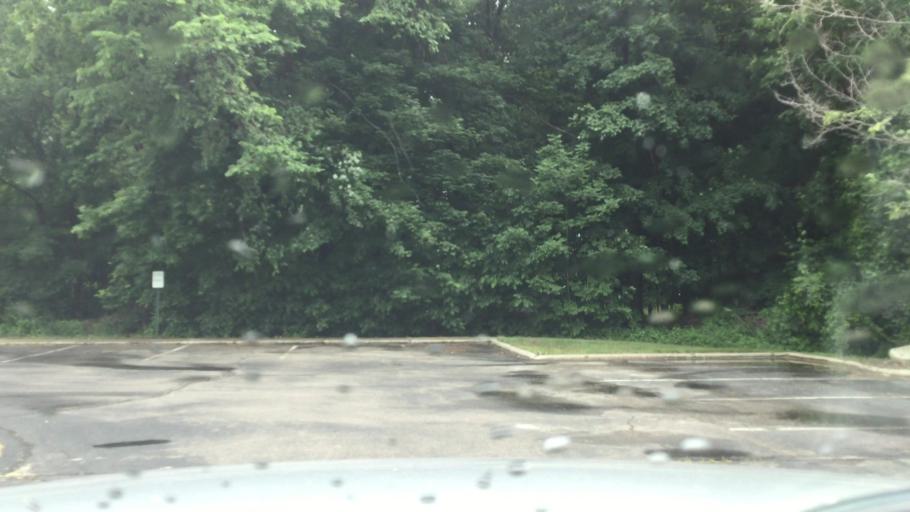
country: US
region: Michigan
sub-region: Lapeer County
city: Lapeer
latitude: 43.0550
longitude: -83.3304
